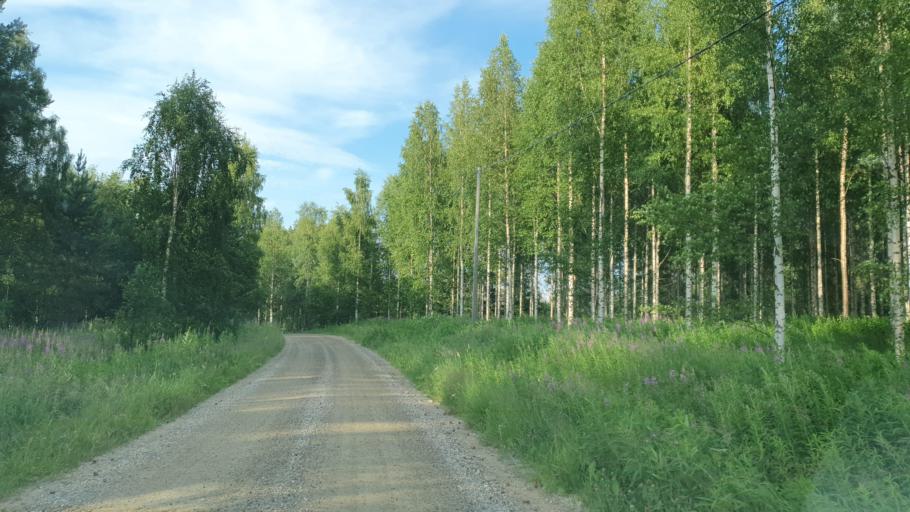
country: FI
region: Kainuu
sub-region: Kehys-Kainuu
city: Kuhmo
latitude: 64.3106
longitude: 29.5612
